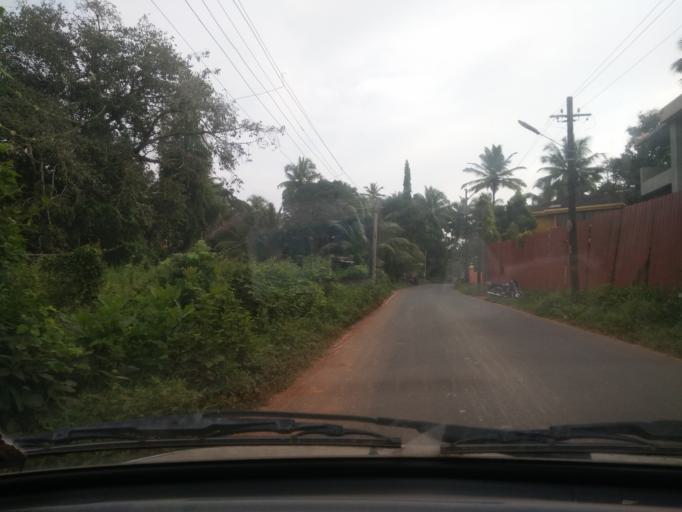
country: IN
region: Goa
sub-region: South Goa
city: Varca
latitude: 15.2221
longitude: 73.9433
